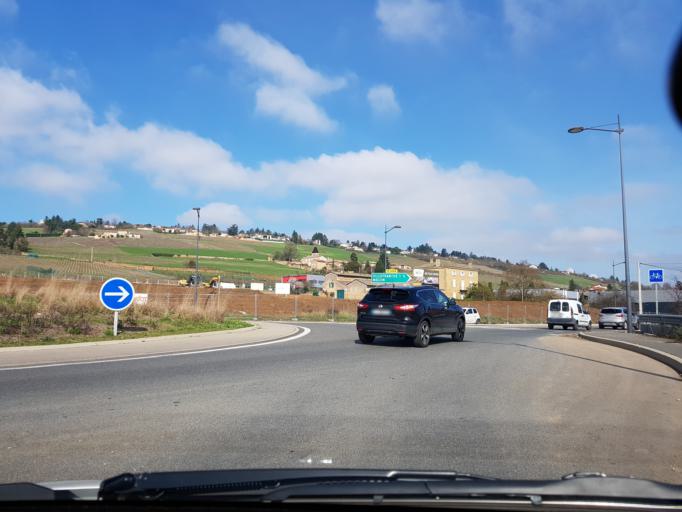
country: FR
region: Rhone-Alpes
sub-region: Departement du Rhone
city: Pommiers
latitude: 45.9598
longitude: 4.7158
